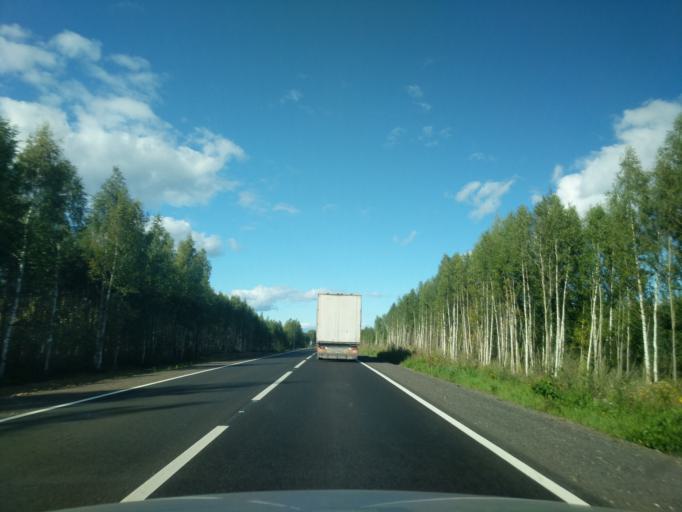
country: RU
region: Kostroma
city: Makar'yev
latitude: 57.9934
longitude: 43.9698
